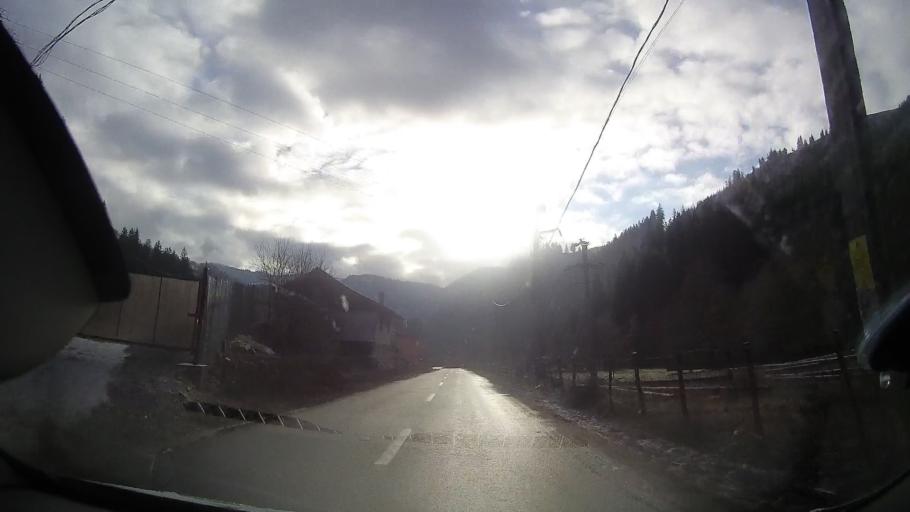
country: RO
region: Alba
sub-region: Comuna Albac
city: Albac
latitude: 46.4651
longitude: 22.9679
